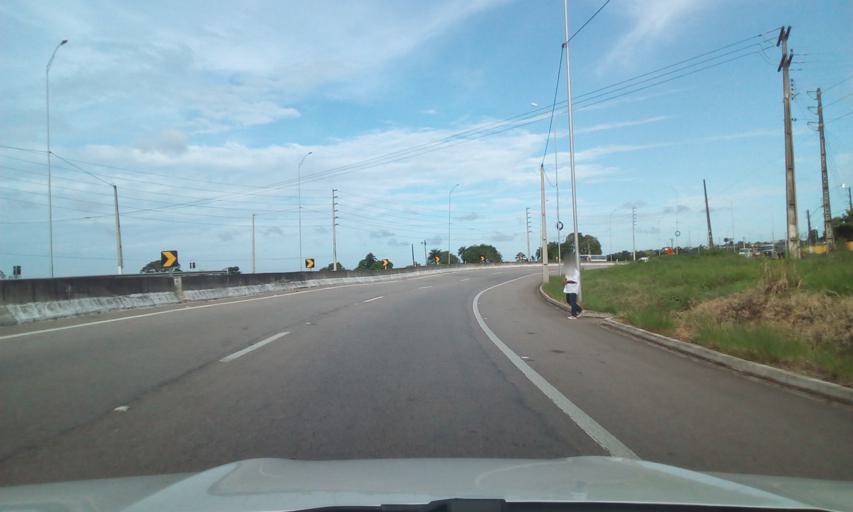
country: BR
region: Paraiba
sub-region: Bayeux
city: Bayeux
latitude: -7.1169
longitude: -34.9503
